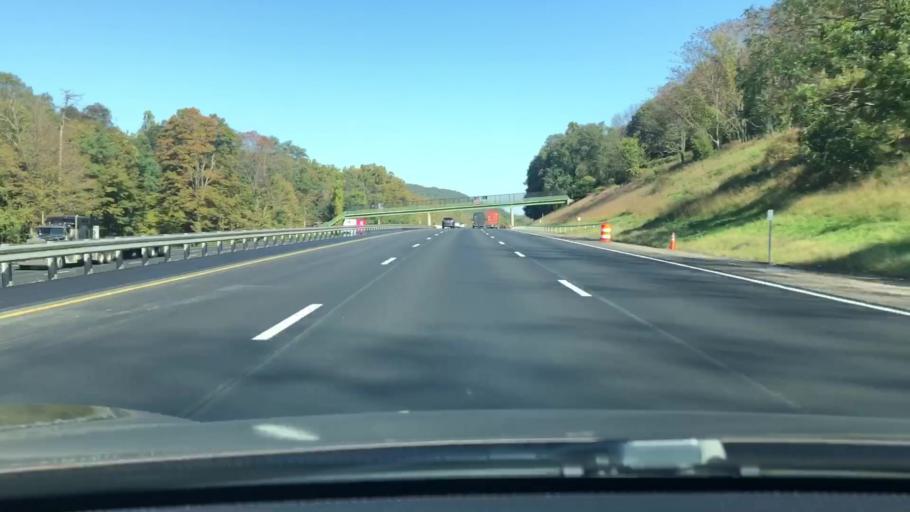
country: US
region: New York
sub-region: Orange County
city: Harriman
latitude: 41.2427
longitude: -74.1708
